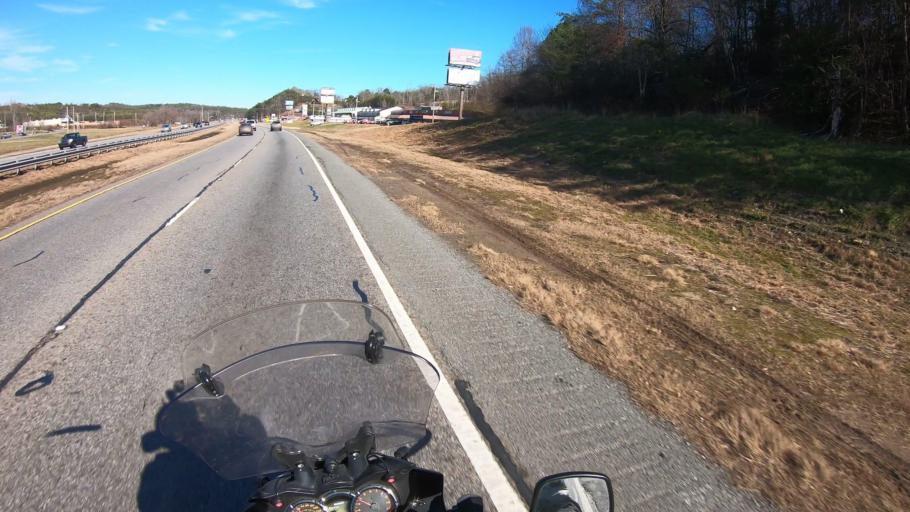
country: US
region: Georgia
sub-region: Fannin County
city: Blue Ridge
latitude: 34.8782
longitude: -84.2974
